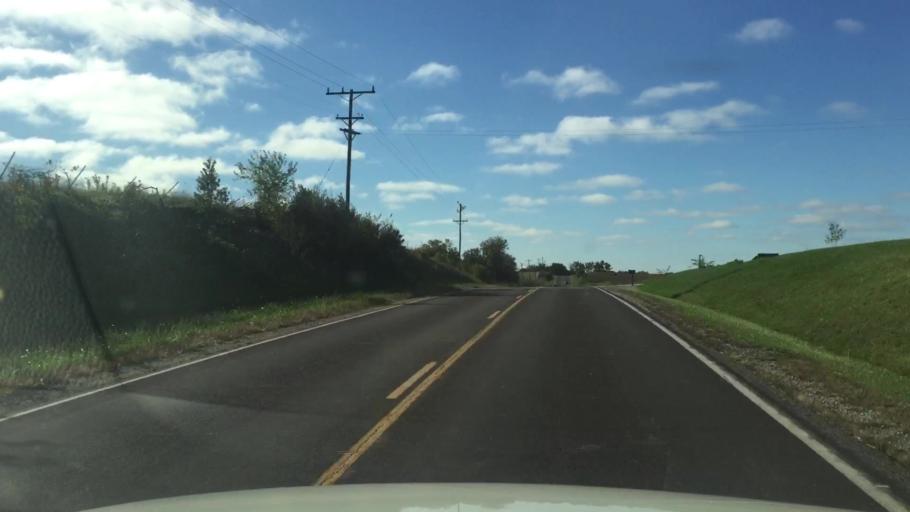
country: US
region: Missouri
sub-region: Howard County
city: New Franklin
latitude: 39.0713
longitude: -92.7459
